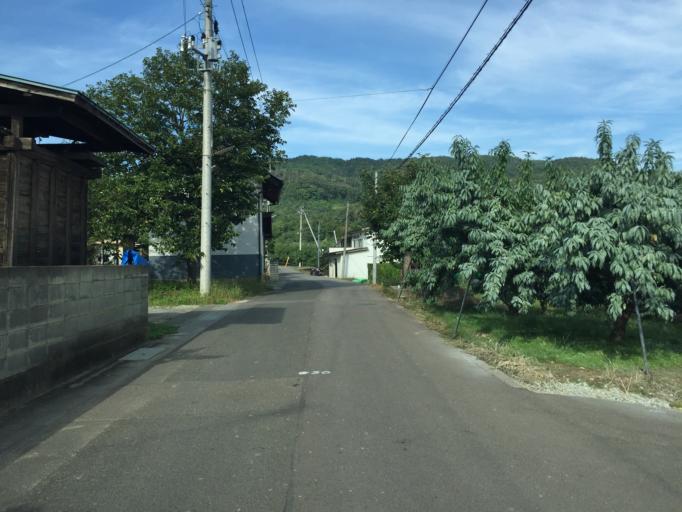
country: JP
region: Fukushima
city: Fukushima-shi
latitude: 37.8360
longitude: 140.4644
